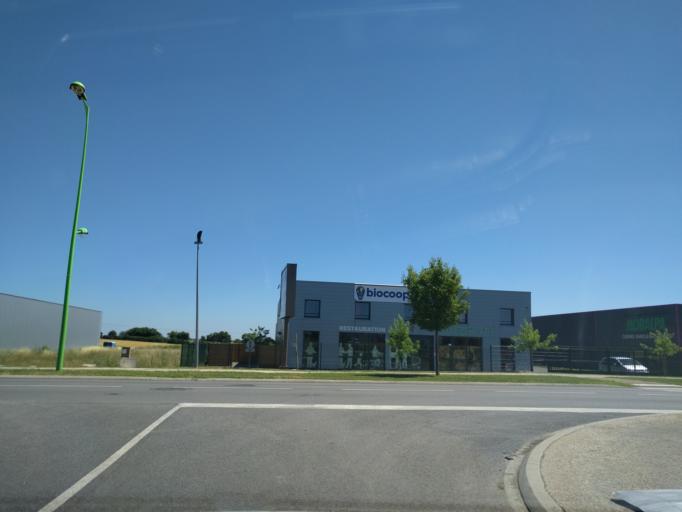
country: FR
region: Poitou-Charentes
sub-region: Departement des Deux-Sevres
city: Chauray
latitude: 46.3374
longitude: -0.3991
